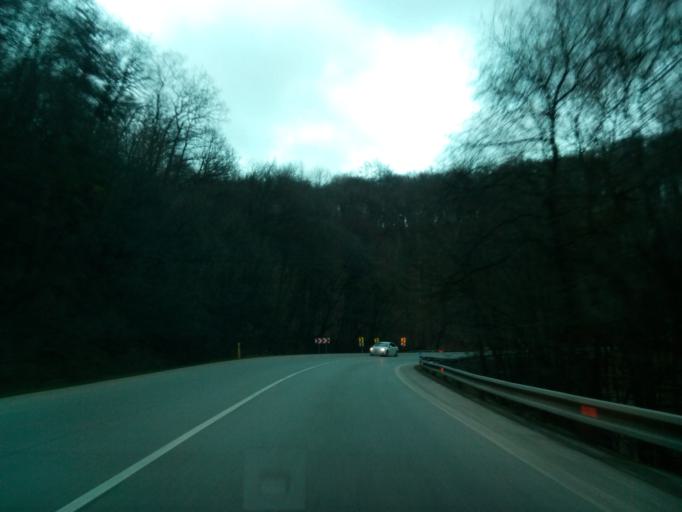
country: SK
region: Kosicky
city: Roznava
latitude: 48.6206
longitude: 20.6330
